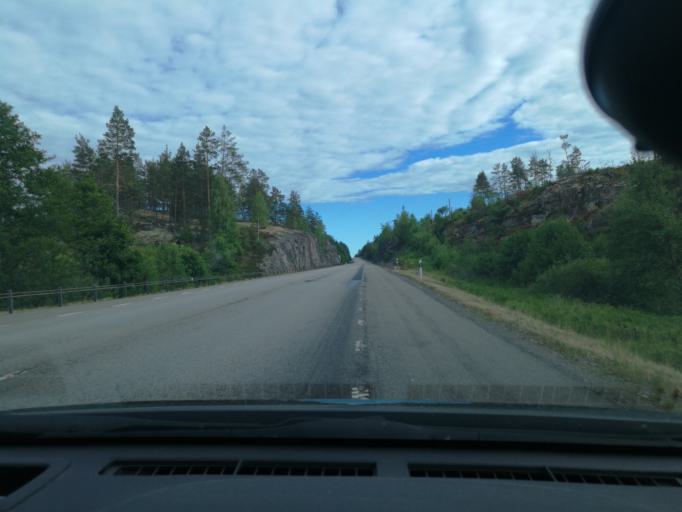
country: SE
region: Kalmar
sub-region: Vasterviks Kommun
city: Ankarsrum
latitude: 57.6012
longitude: 16.4803
